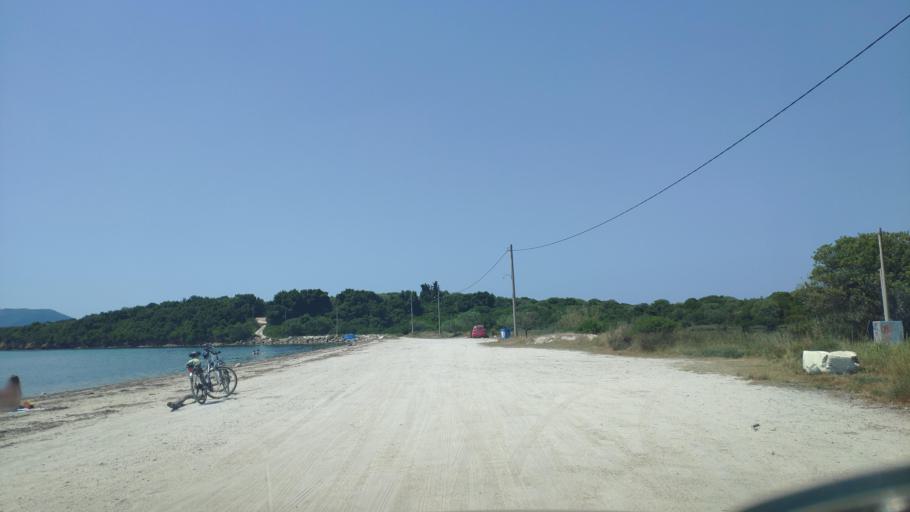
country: GR
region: Epirus
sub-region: Nomos Artas
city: Aneza
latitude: 39.0116
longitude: 20.9257
